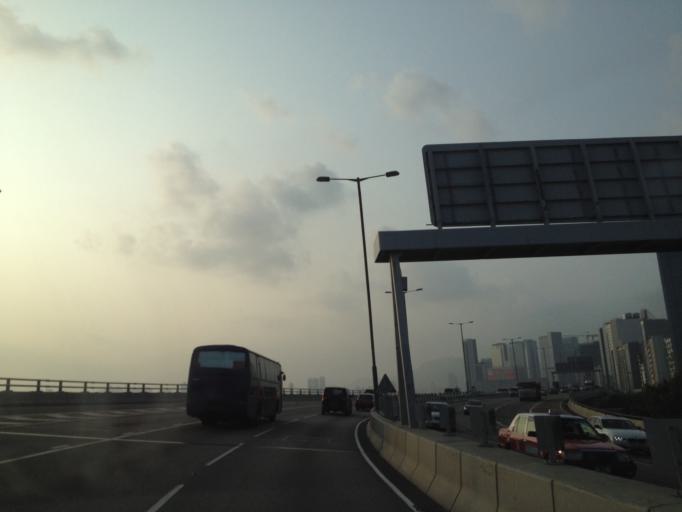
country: HK
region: Kowloon City
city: Kowloon
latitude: 22.3060
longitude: 114.2225
